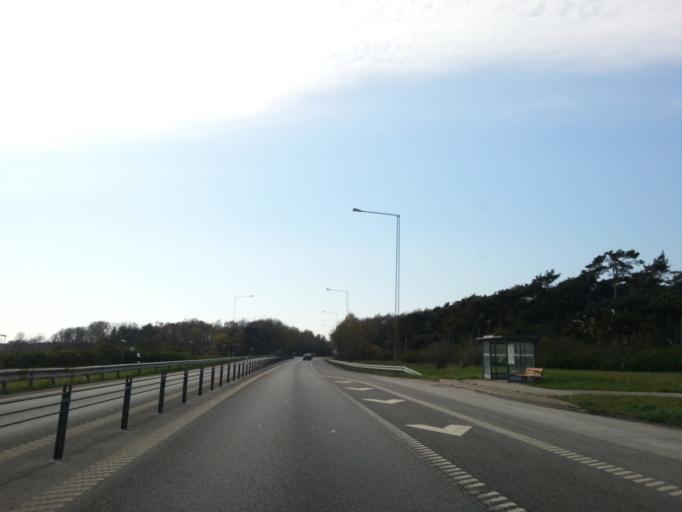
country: SE
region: Skane
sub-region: Trelleborgs Kommun
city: Skare
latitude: 55.3769
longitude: 13.0999
